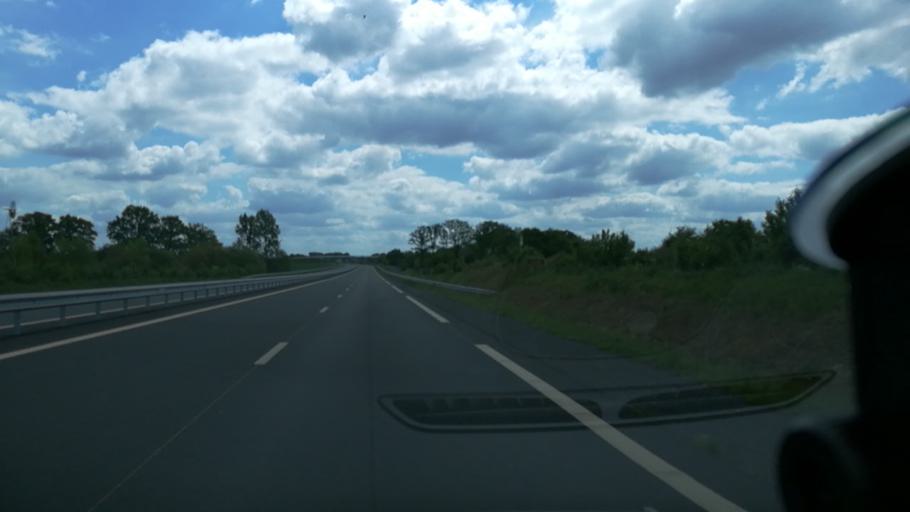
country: FR
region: Brittany
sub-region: Departement d'Ille-et-Vilaine
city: Retiers
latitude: 47.8783
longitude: -1.3635
